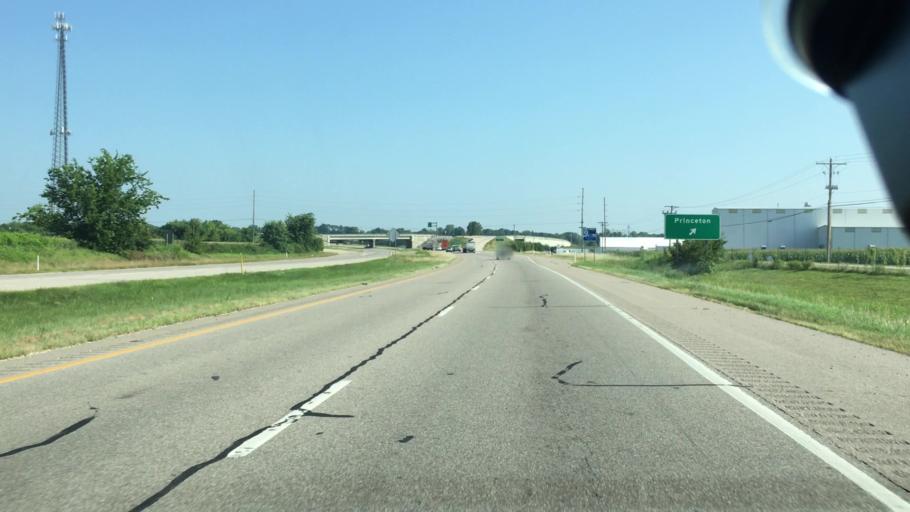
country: US
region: Indiana
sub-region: Gibson County
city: Princeton
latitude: 38.3079
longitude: -87.5673
